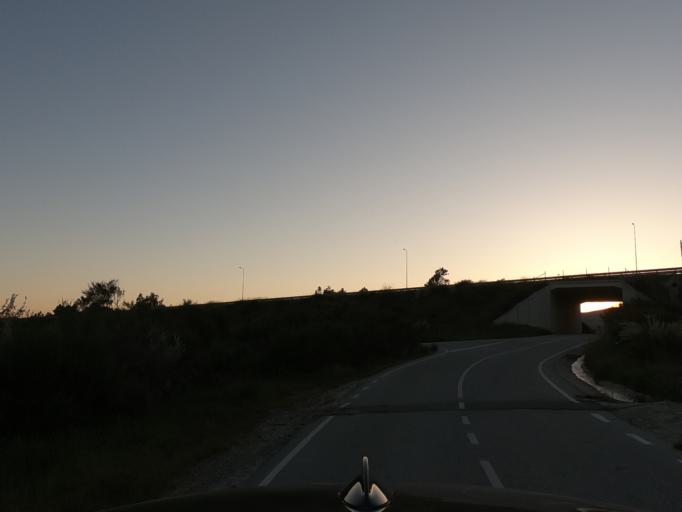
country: PT
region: Vila Real
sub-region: Vila Real
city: Vila Real
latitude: 41.3159
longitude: -7.6609
